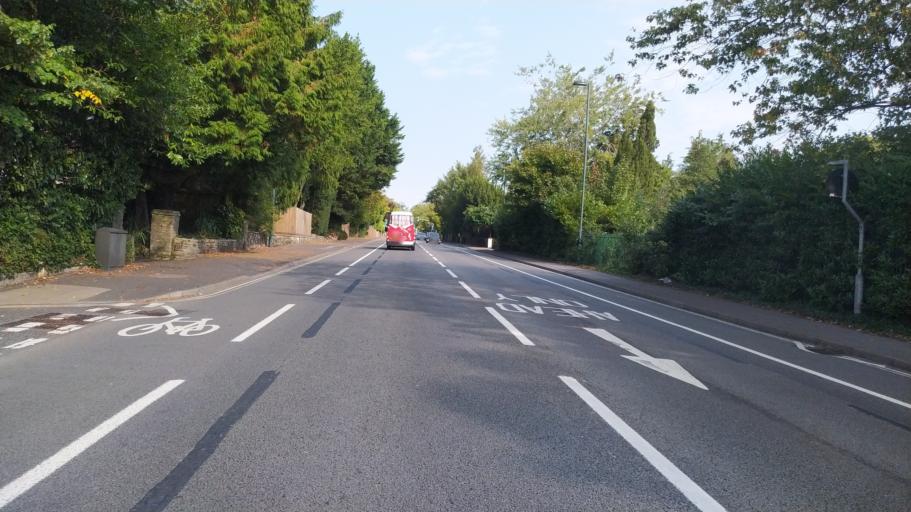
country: GB
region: England
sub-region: Southampton
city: Southampton
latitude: 50.9372
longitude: -1.4066
